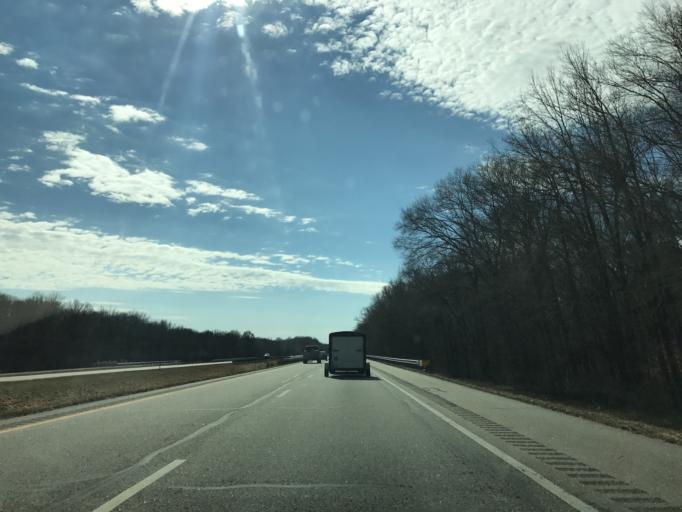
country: US
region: Delaware
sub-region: New Castle County
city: Townsend
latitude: 39.2936
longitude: -75.8537
